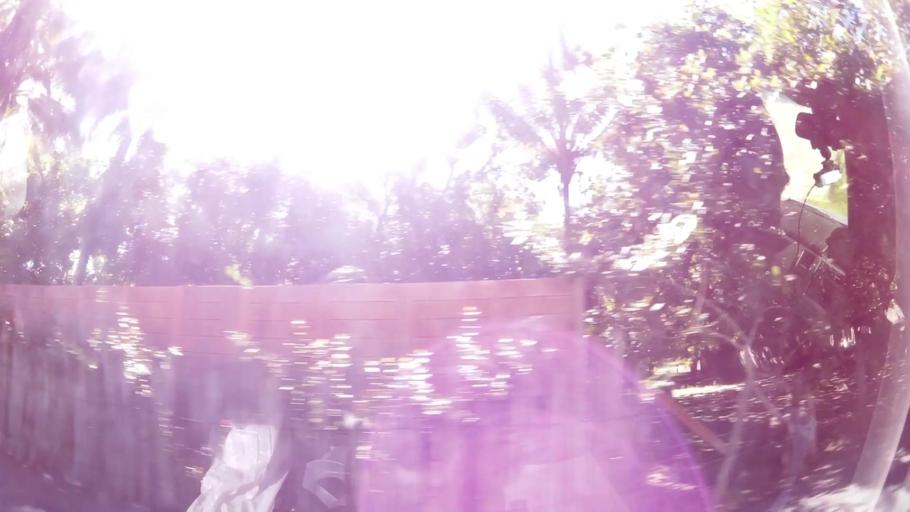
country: GT
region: Escuintla
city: Iztapa
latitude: 13.9322
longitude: -90.7032
